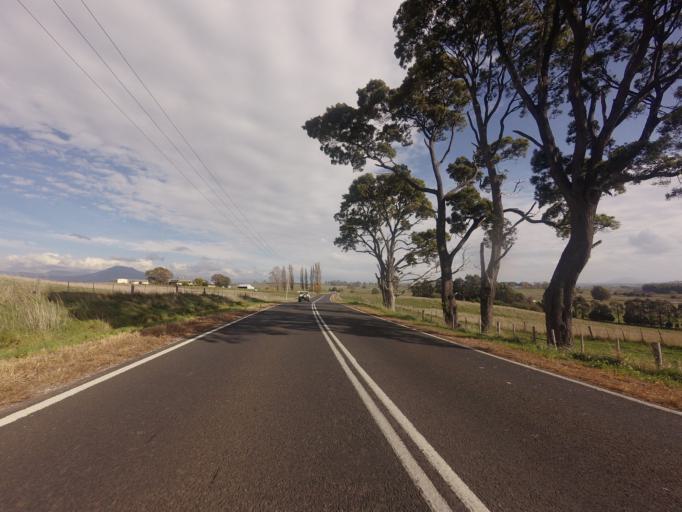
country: AU
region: Tasmania
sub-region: Meander Valley
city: Deloraine
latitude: -41.5205
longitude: 146.7210
